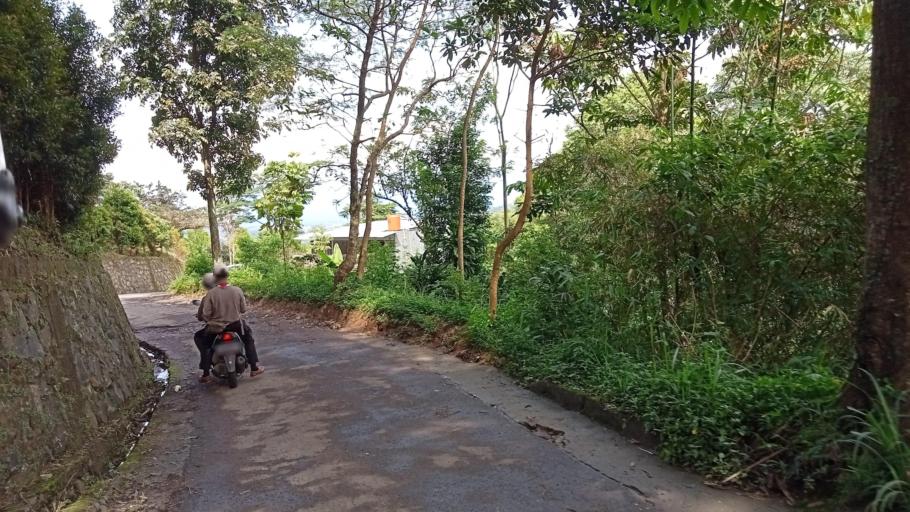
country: ID
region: West Java
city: Caringin
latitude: -6.6412
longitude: 106.9077
